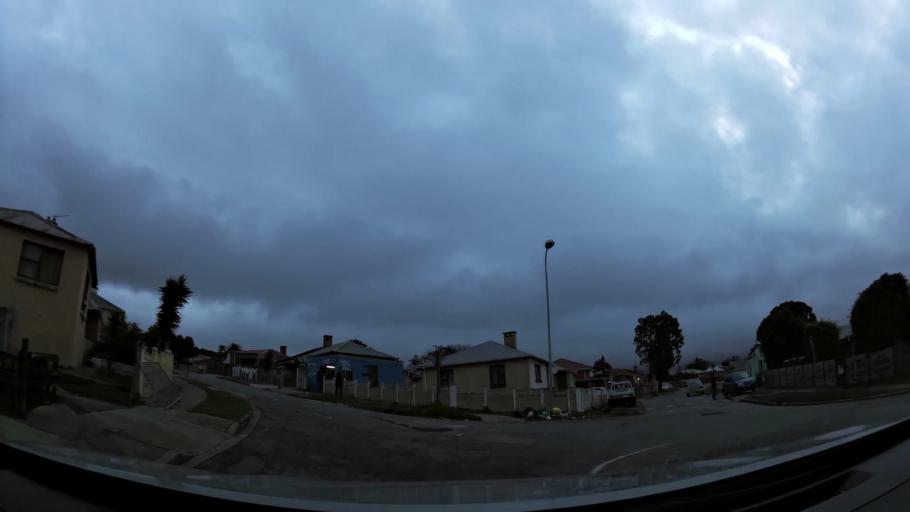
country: ZA
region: Eastern Cape
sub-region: Nelson Mandela Bay Metropolitan Municipality
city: Port Elizabeth
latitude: -33.9424
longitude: 25.5934
